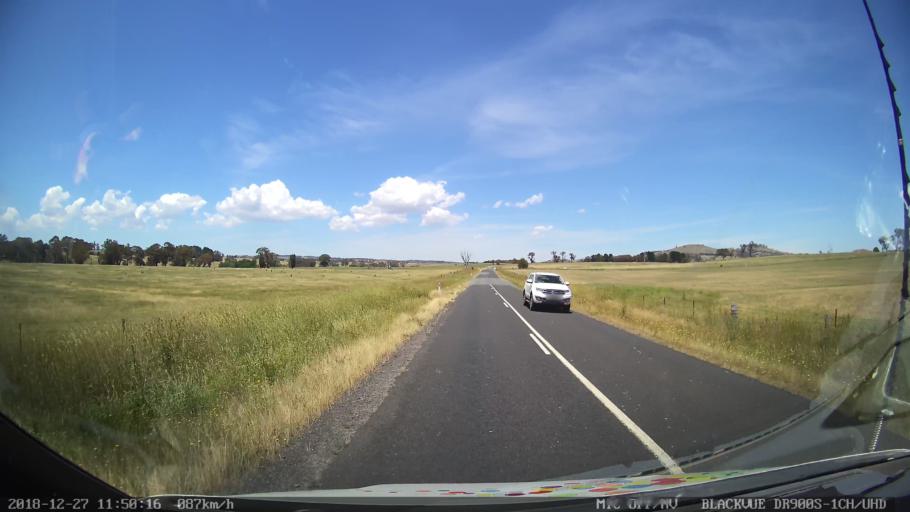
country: AU
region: New South Wales
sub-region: Bathurst Regional
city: Perthville
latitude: -33.6307
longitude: 149.4319
